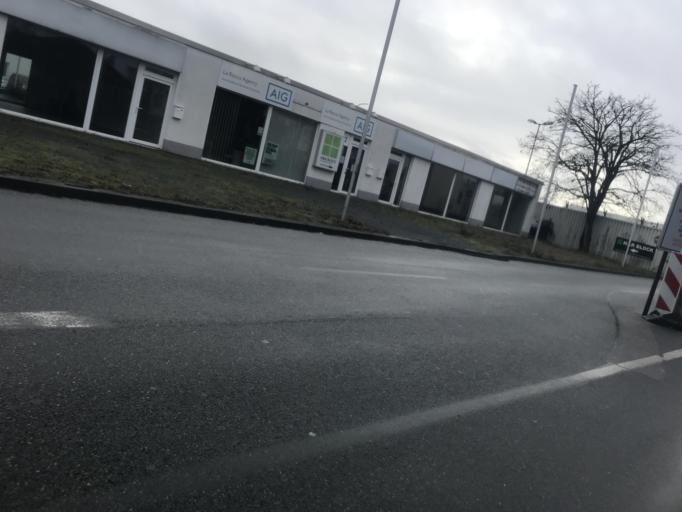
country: DE
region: Rheinland-Pfalz
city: Mainz
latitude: 50.0144
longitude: 8.2872
